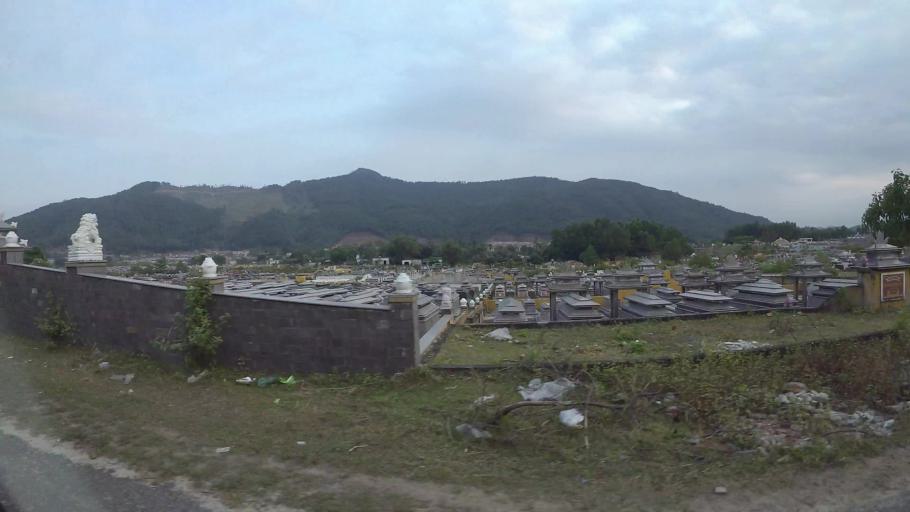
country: VN
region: Da Nang
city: Lien Chieu
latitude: 16.0618
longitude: 108.1211
